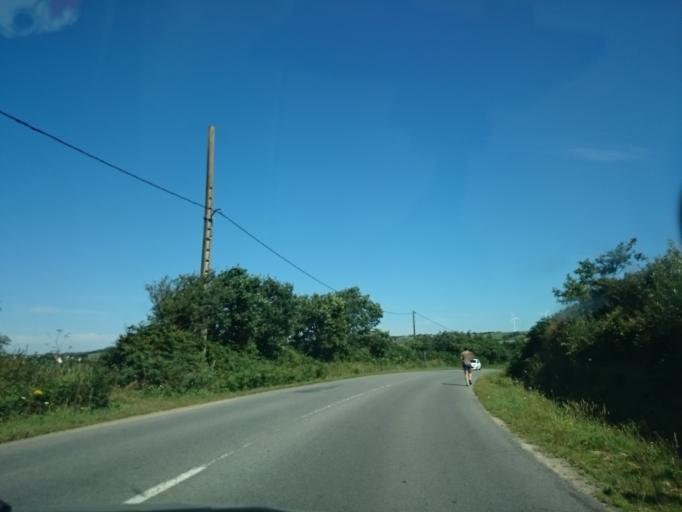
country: FR
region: Brittany
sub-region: Departement du Finistere
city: Saint-Renan
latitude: 48.4375
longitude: -4.6467
